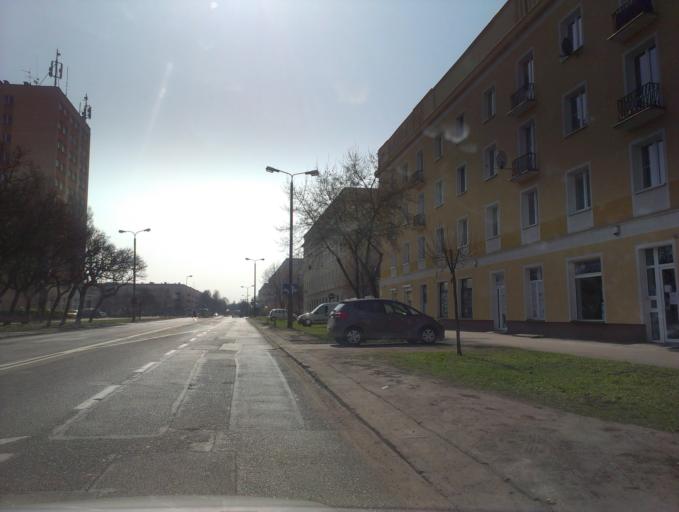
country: PL
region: Kujawsko-Pomorskie
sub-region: Bydgoszcz
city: Bydgoszcz
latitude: 53.1416
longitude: 18.0301
